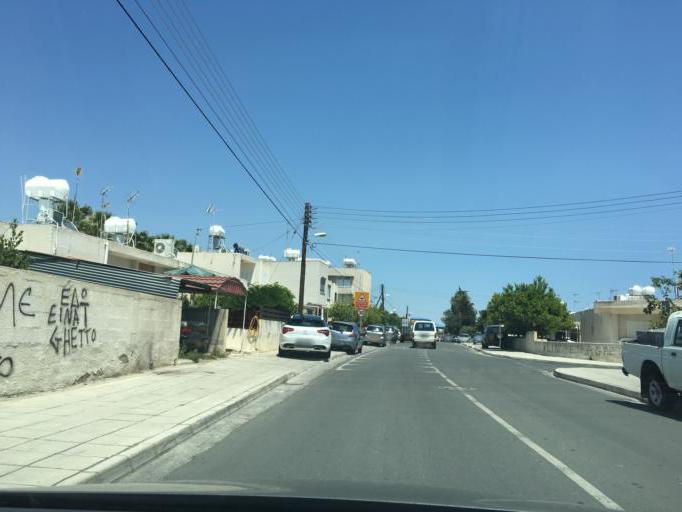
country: CY
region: Limassol
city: Limassol
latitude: 34.6975
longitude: 33.0654
